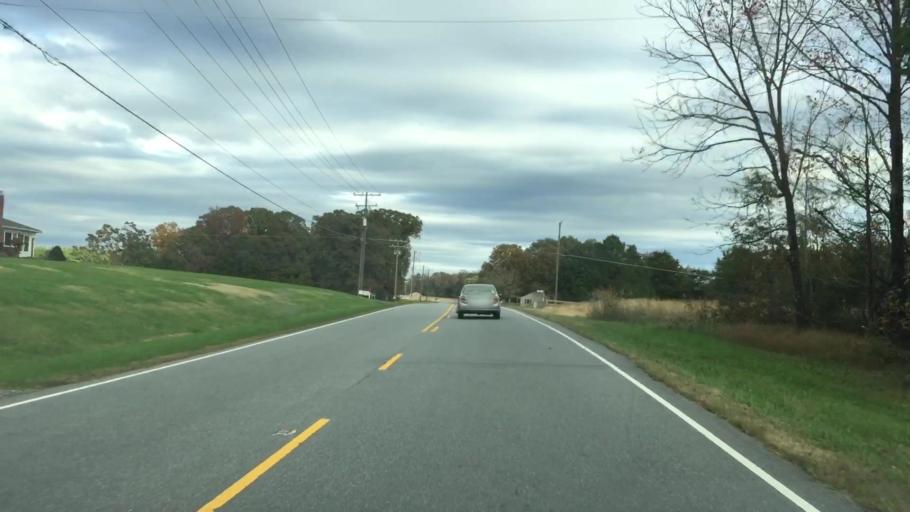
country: US
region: North Carolina
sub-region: Rockingham County
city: Wentworth
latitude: 36.2747
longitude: -79.7776
